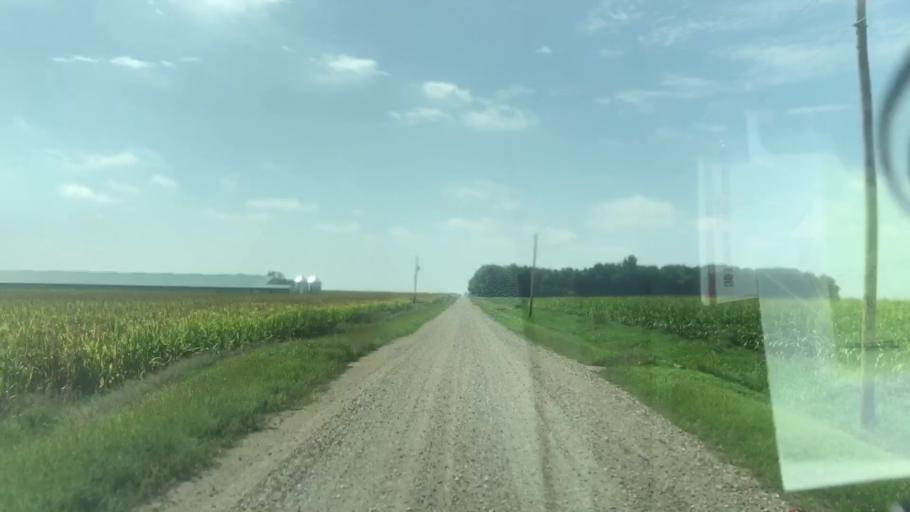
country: US
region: Iowa
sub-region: O'Brien County
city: Sheldon
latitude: 43.1959
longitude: -95.9416
